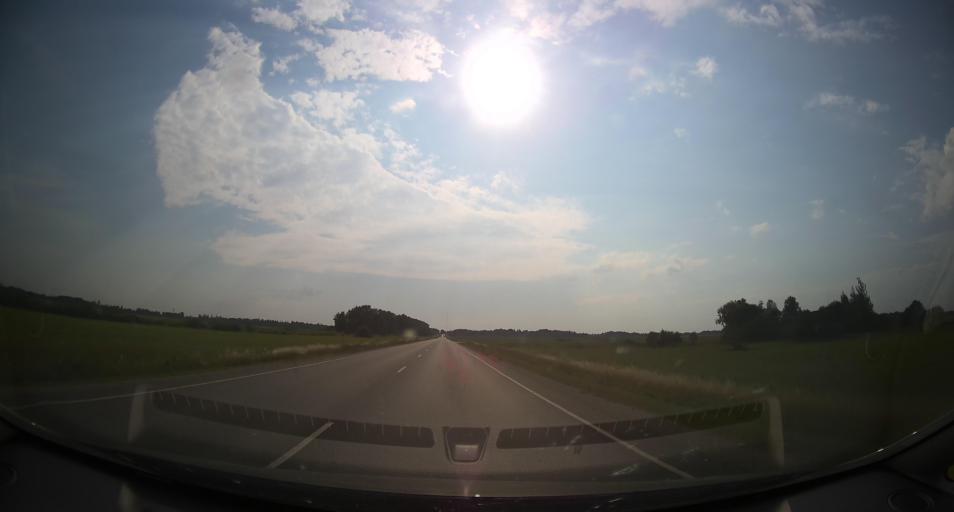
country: EE
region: Laeaene
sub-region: Lihula vald
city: Lihula
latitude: 58.7319
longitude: 23.9719
